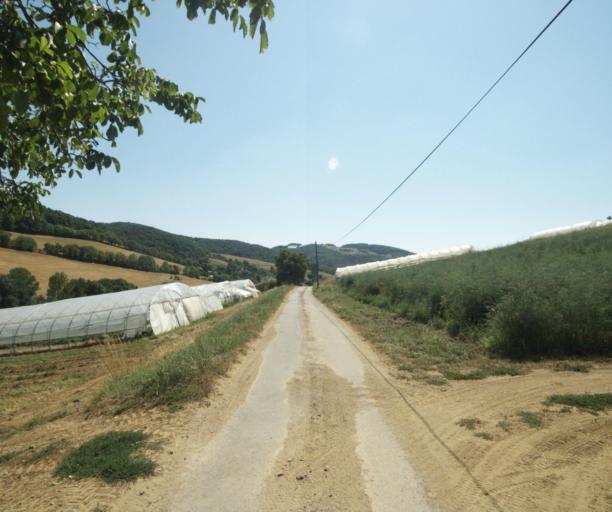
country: FR
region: Rhone-Alpes
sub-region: Departement du Rhone
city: Courzieu
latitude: 45.7211
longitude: 4.5377
